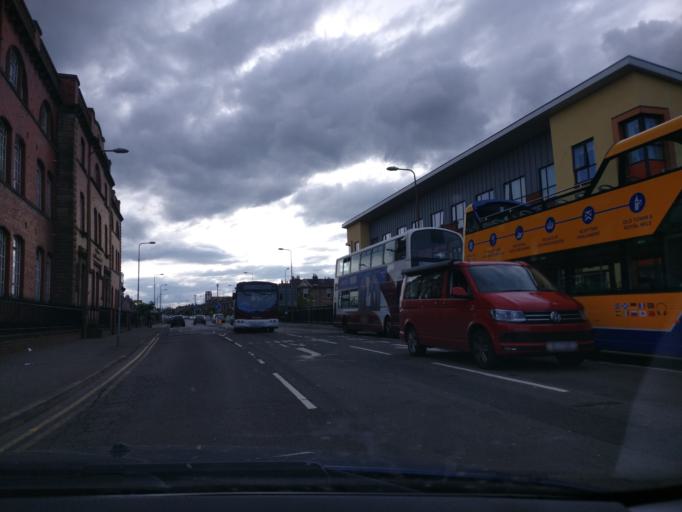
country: GB
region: Scotland
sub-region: West Lothian
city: Seafield
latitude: 55.9575
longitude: -3.1235
